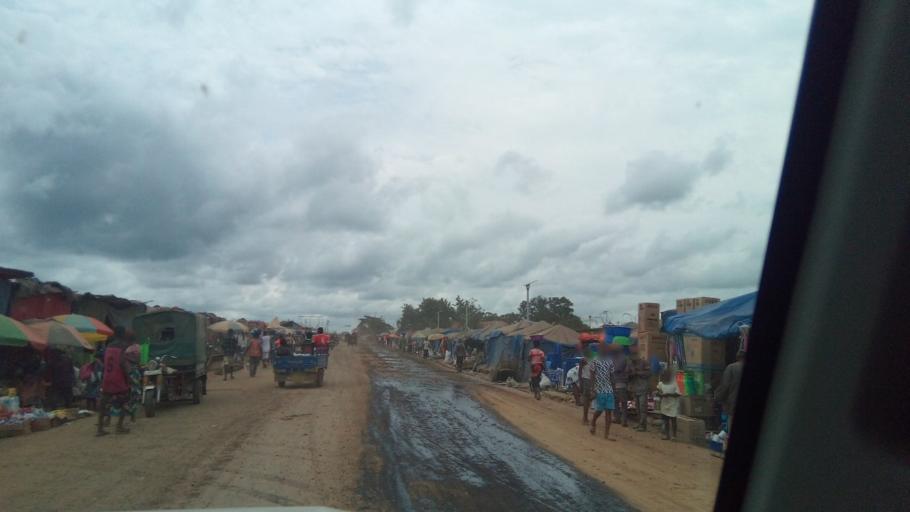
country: AO
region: Zaire
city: Mbanza Congo
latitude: -5.8342
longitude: 14.0754
